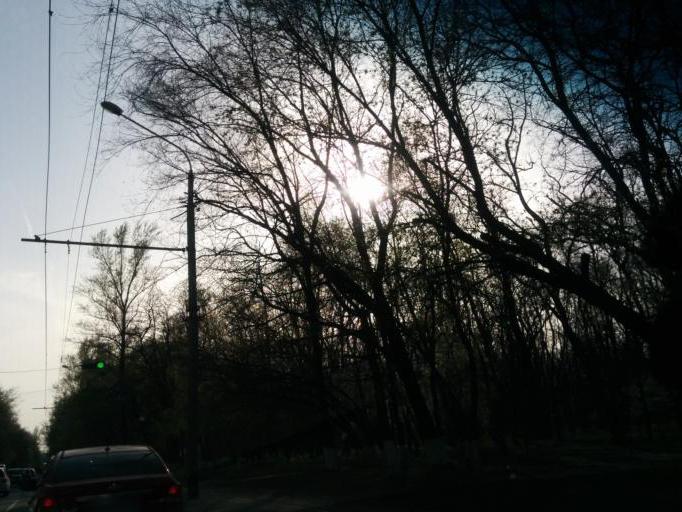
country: RU
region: Rostov
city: Aksay
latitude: 47.2655
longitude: 39.8140
